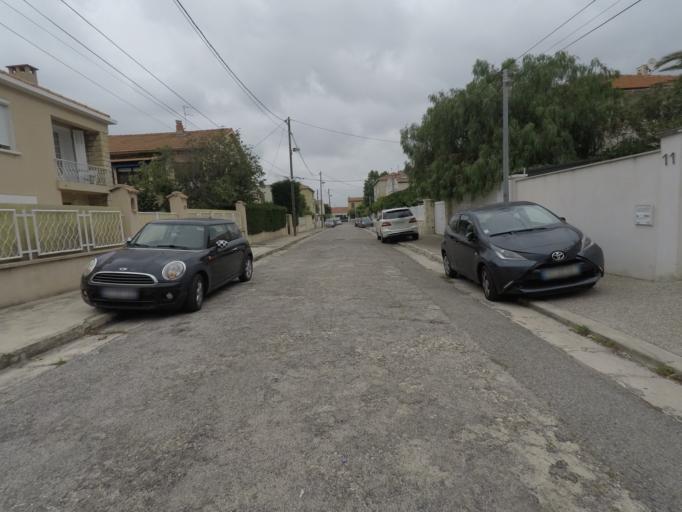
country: FR
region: Provence-Alpes-Cote d'Azur
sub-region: Departement des Bouches-du-Rhone
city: Marseille 09
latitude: 43.2631
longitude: 5.4060
